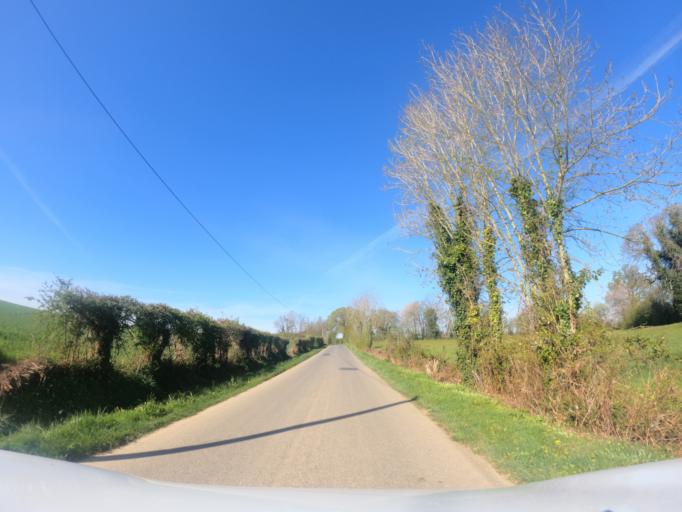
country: FR
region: Pays de la Loire
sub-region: Departement de la Vendee
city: La Tardiere
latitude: 46.6906
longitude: -0.7355
